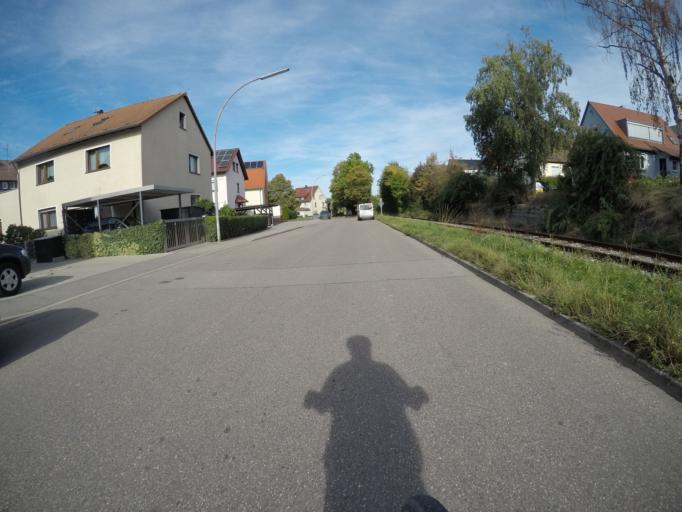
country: DE
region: Baden-Wuerttemberg
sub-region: Regierungsbezirk Stuttgart
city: Schwieberdingen
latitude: 48.8578
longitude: 9.0919
